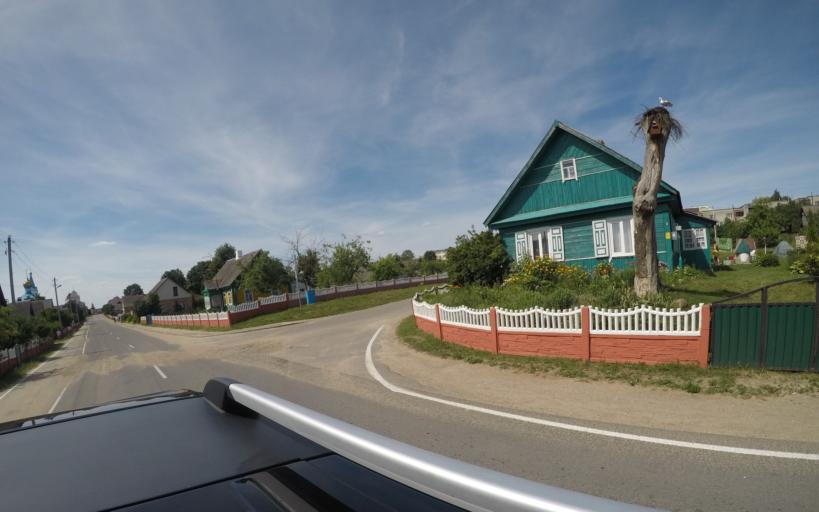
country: BY
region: Grodnenskaya
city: Hal'shany
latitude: 54.2547
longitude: 26.0170
